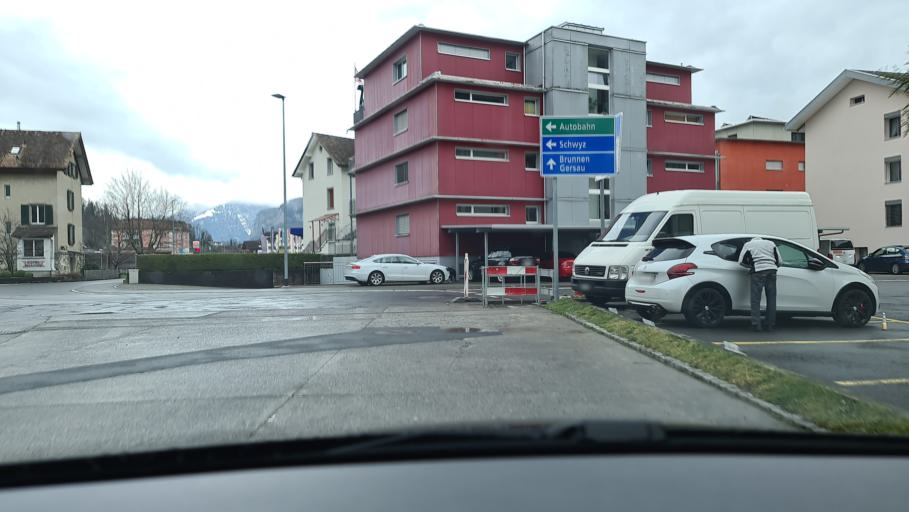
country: CH
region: Schwyz
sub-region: Bezirk Schwyz
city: Ingenbohl
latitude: 47.0014
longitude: 8.6107
